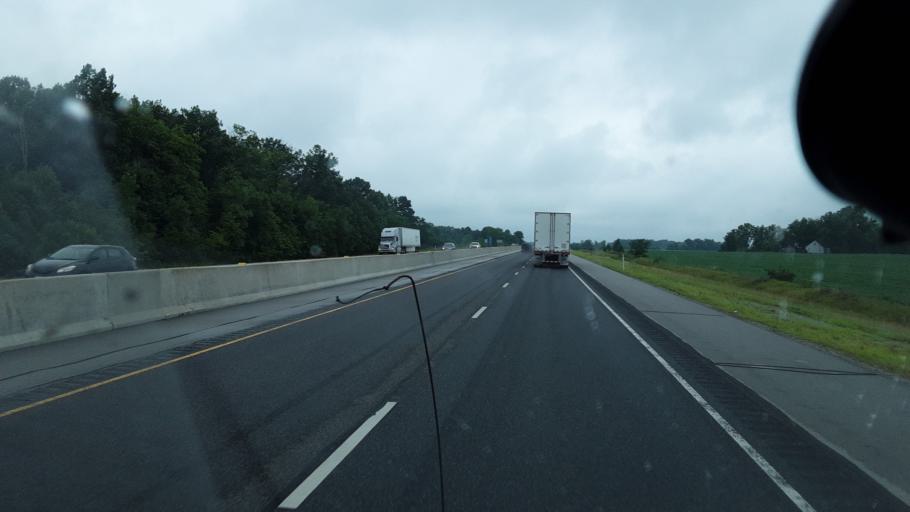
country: US
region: Indiana
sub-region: Wells County
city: Ossian
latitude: 40.9782
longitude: -85.1086
